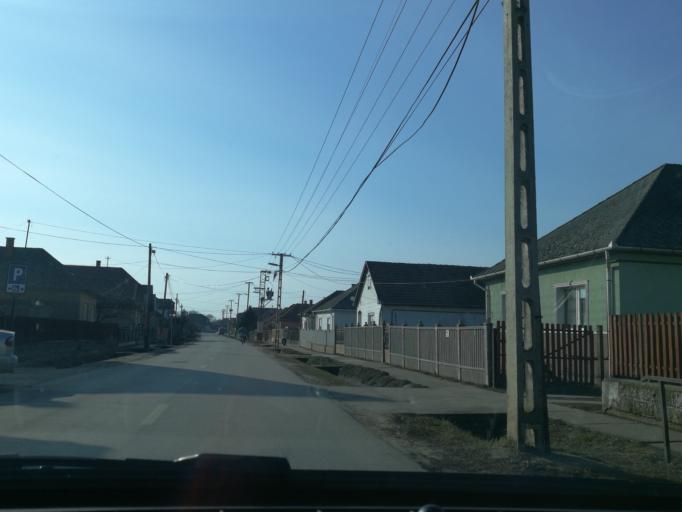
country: HU
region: Szabolcs-Szatmar-Bereg
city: Apagy
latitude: 48.0209
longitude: 21.9609
